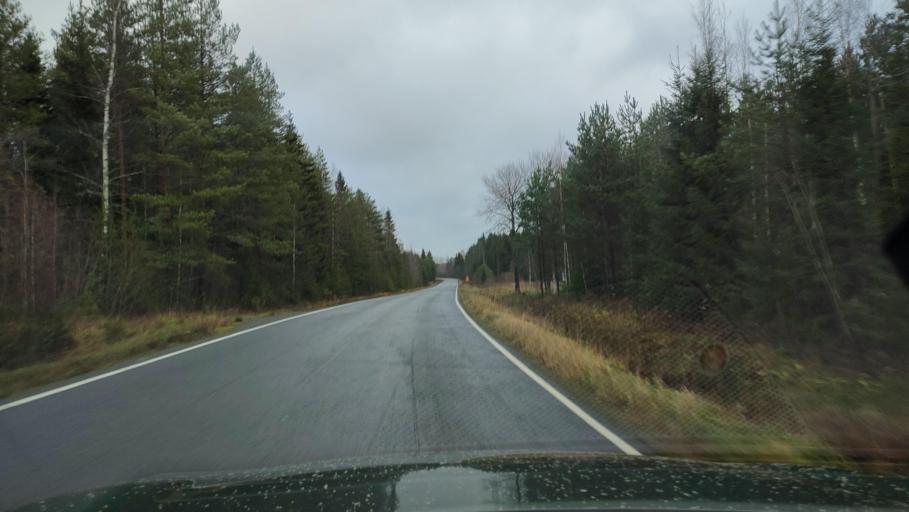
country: FI
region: Southern Ostrobothnia
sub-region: Suupohja
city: Karijoki
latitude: 62.3479
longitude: 21.5369
